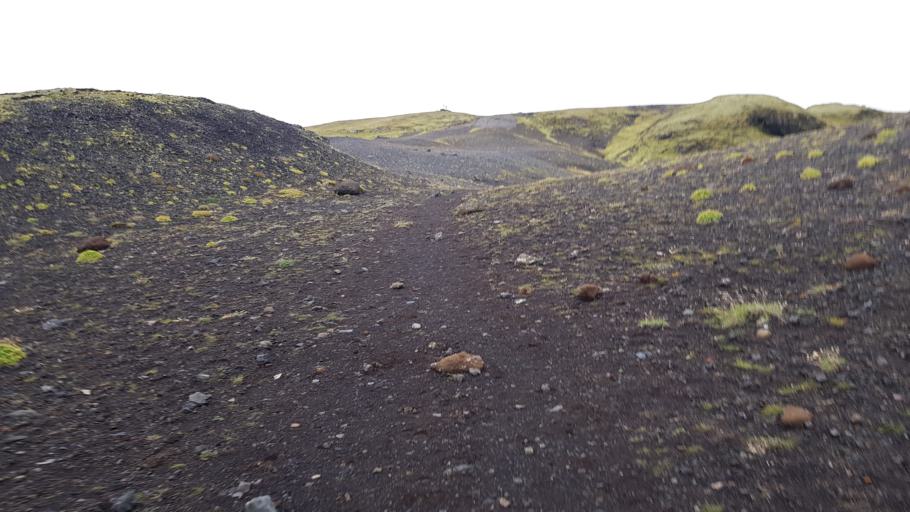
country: IS
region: South
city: Vestmannaeyjar
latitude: 63.5289
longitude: -18.8481
